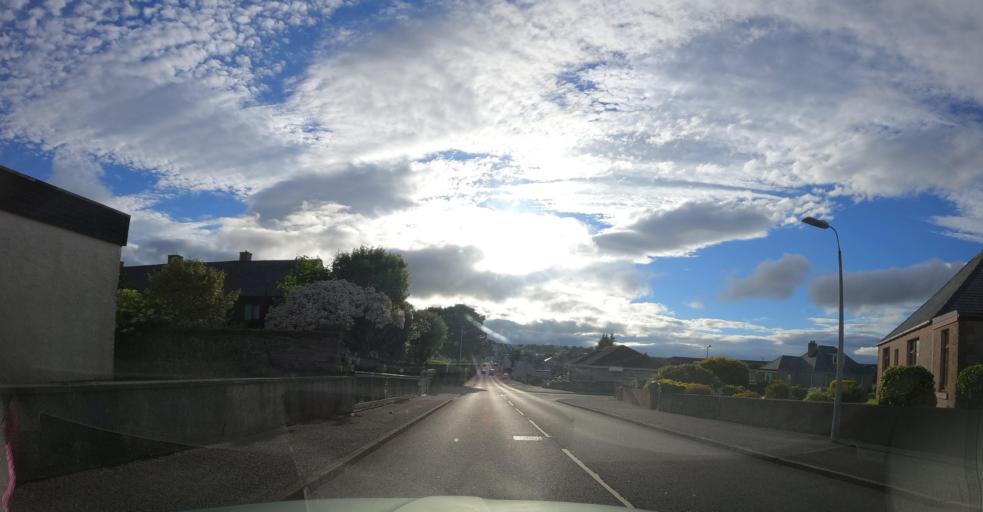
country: GB
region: Scotland
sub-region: Eilean Siar
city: Isle of Lewis
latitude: 58.2184
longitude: -6.3794
